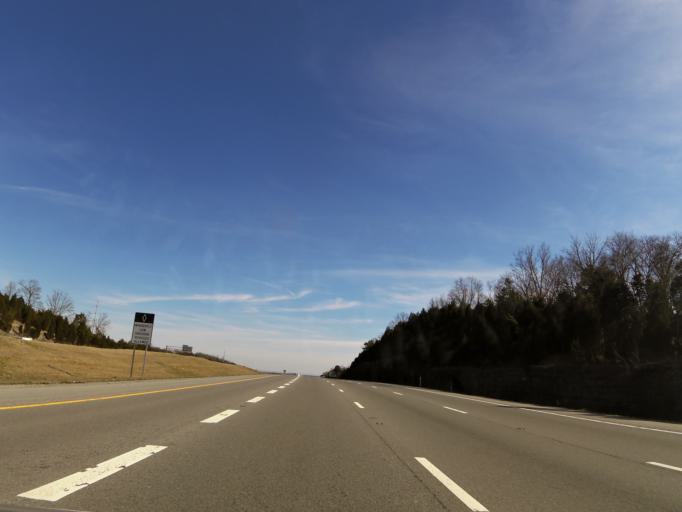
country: US
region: Tennessee
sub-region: Rutherford County
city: Smyrna
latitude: 35.9606
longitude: -86.5612
